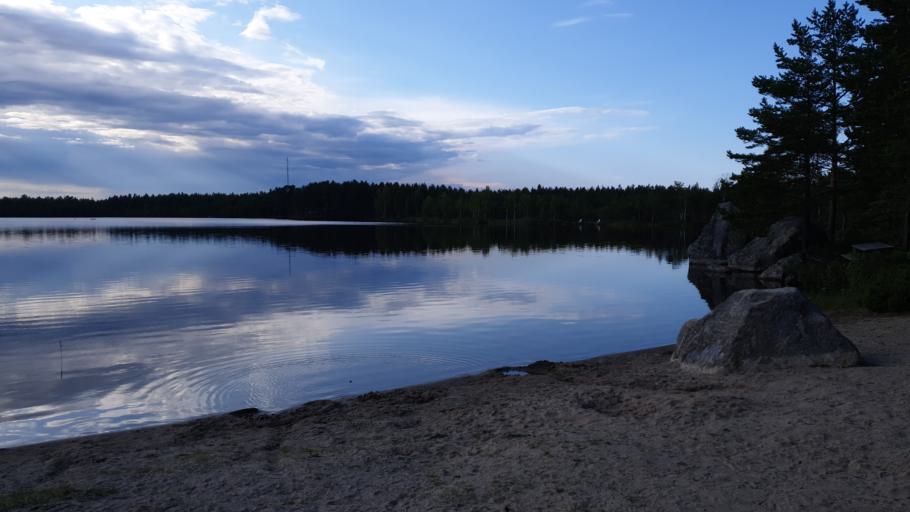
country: SE
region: Gaevleborg
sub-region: Soderhamns Kommun
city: Marielund
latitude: 61.4261
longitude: 17.1543
